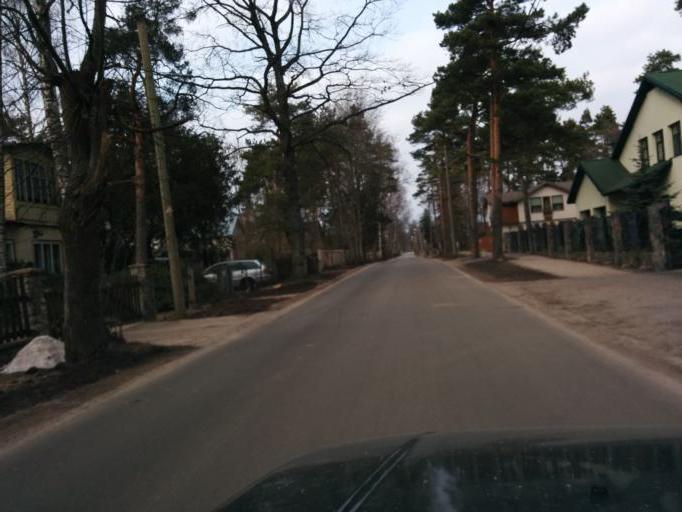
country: LV
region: Jurmala
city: Jurmala
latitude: 56.9555
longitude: 23.7239
